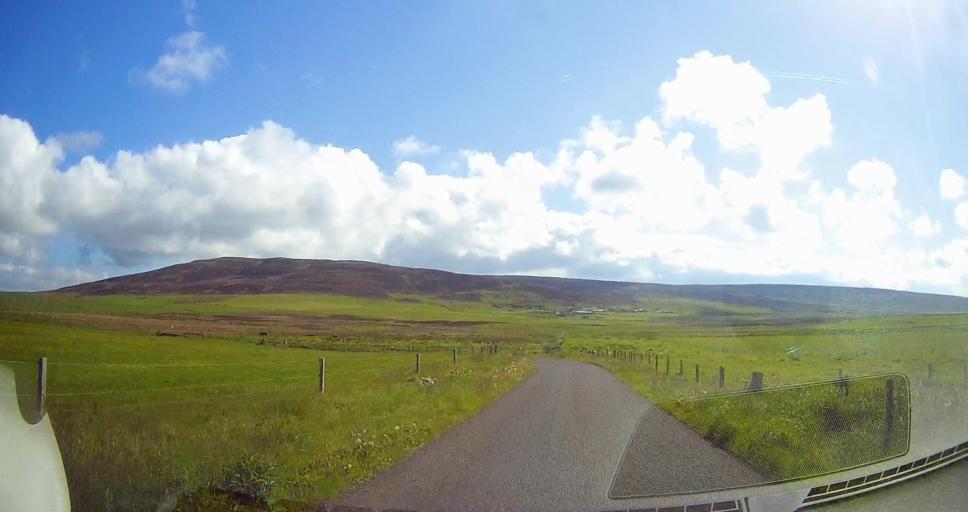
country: GB
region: Scotland
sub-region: Orkney Islands
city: Stromness
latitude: 58.9858
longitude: -3.1470
